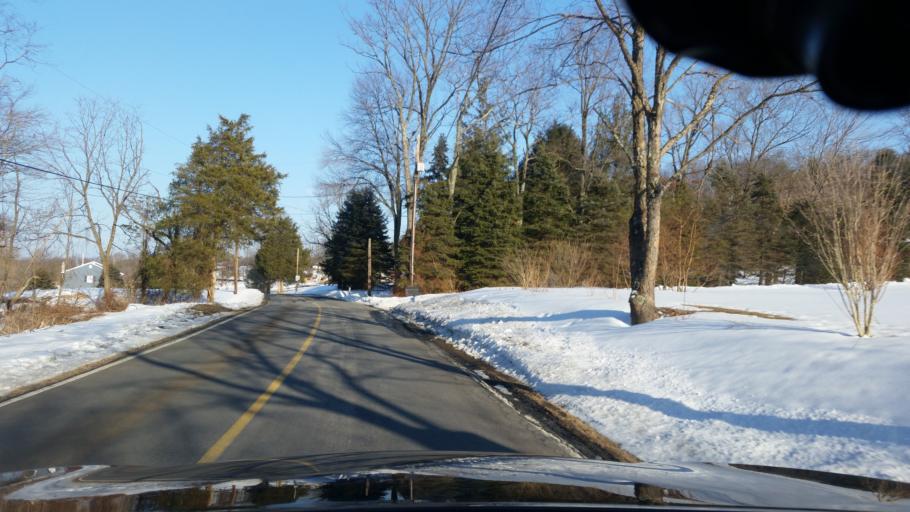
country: US
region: Pennsylvania
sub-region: Perry County
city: Marysville
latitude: 40.3238
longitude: -76.9917
